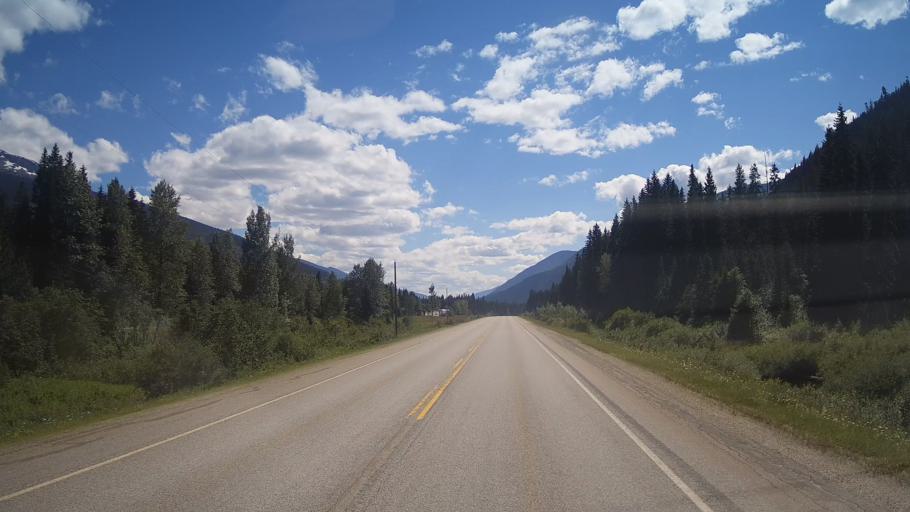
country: CA
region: Alberta
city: Jasper Park Lodge
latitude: 52.5790
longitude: -119.0966
